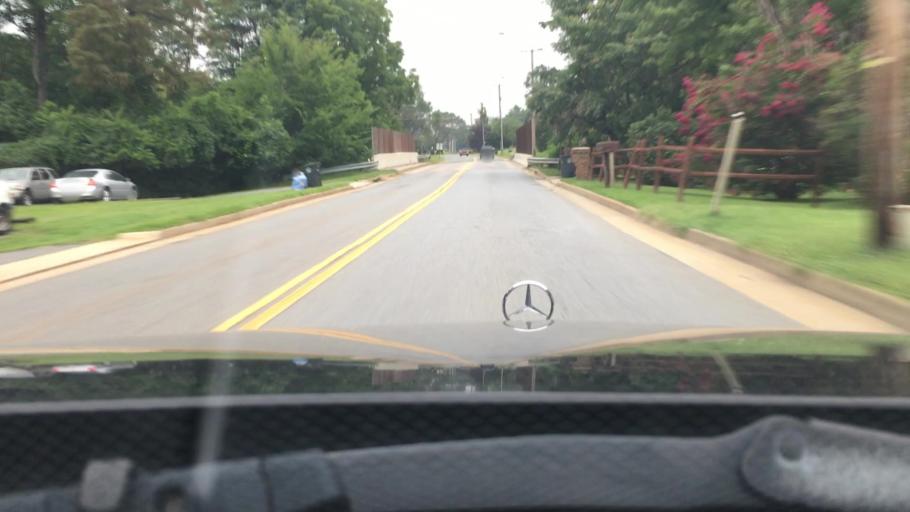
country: US
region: Virginia
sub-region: Campbell County
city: Timberlake
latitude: 37.3680
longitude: -79.2265
